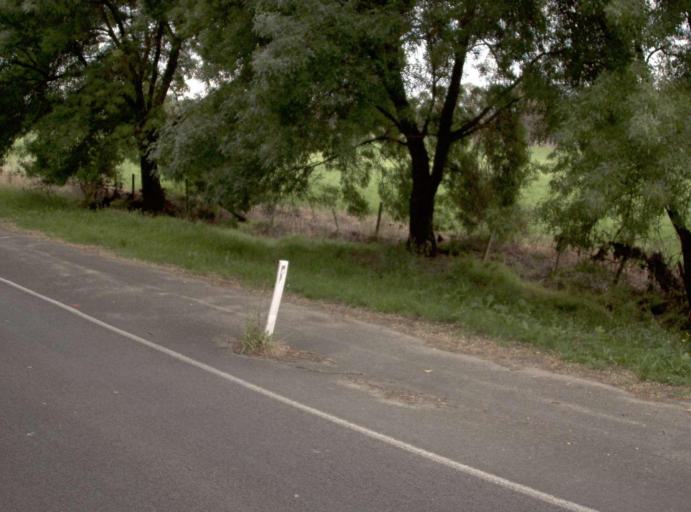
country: AU
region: Victoria
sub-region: East Gippsland
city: Bairnsdale
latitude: -37.8186
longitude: 147.6195
